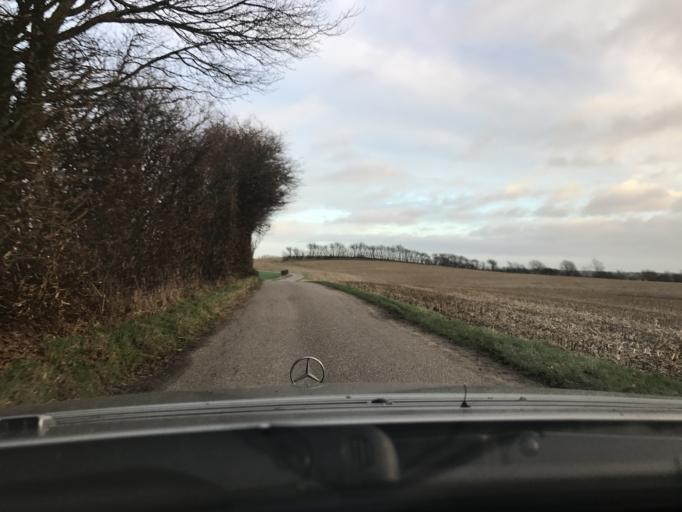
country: DK
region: South Denmark
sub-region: Sonderborg Kommune
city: Nordborg
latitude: 55.0456
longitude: 9.6542
